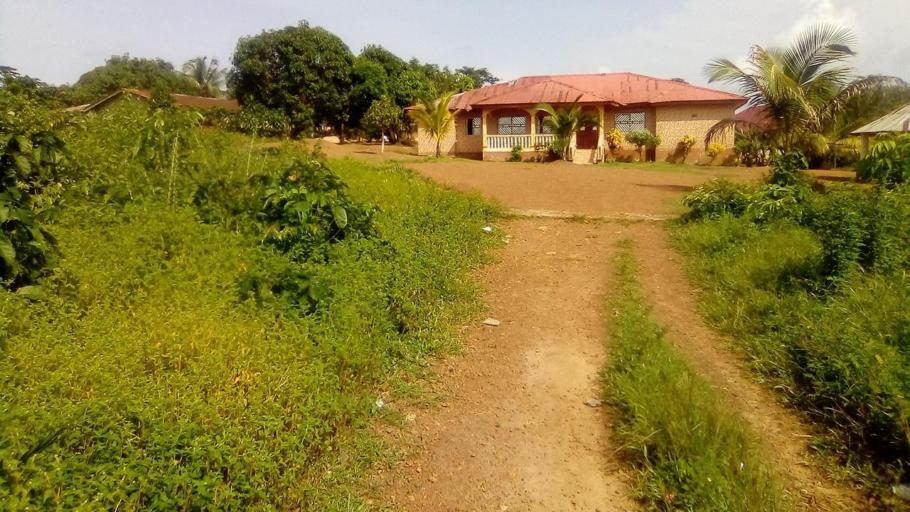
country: SL
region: Southern Province
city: Pujehun
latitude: 7.3640
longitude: -11.7258
